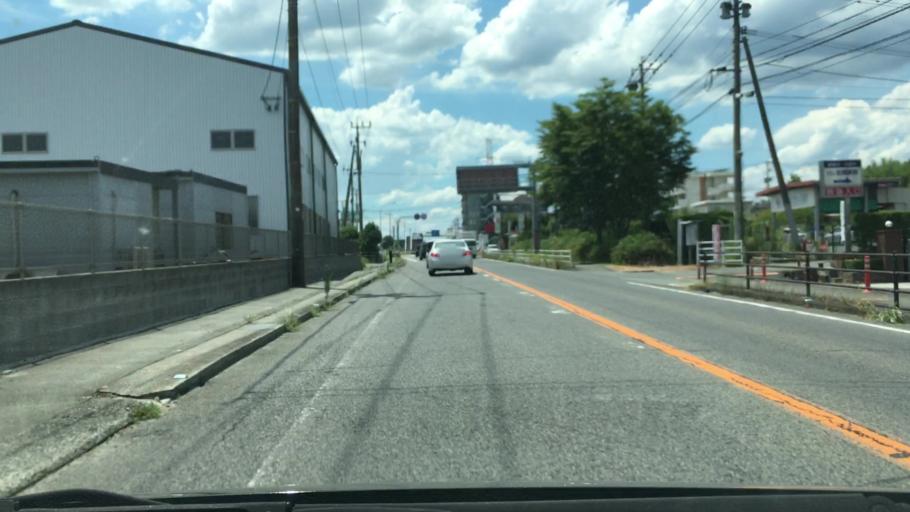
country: JP
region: Saga Prefecture
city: Tosu
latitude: 33.3533
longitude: 130.4709
